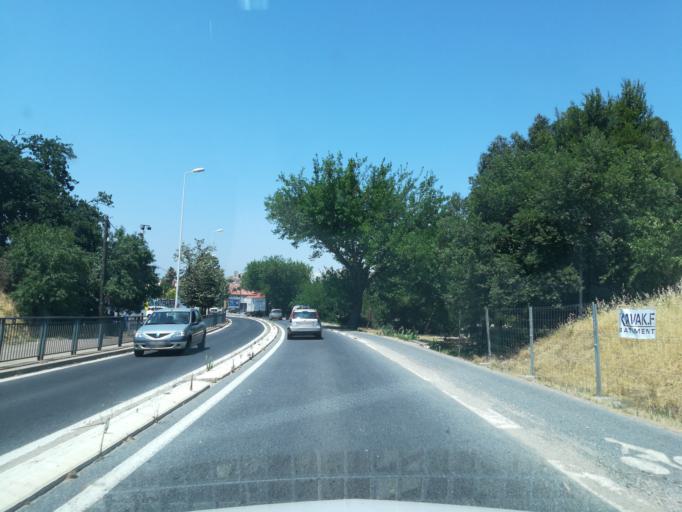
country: FR
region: Languedoc-Roussillon
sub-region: Departement des Pyrenees-Orientales
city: Perpignan
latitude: 42.6849
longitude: 2.8963
